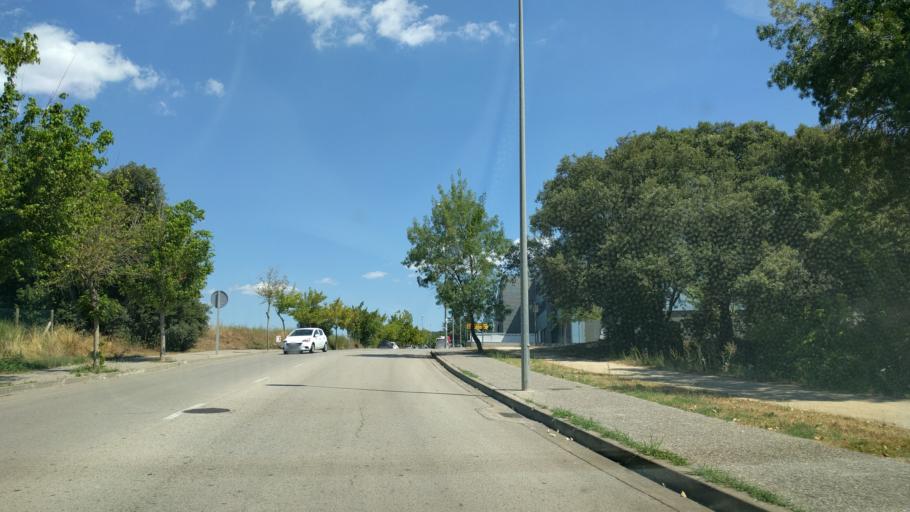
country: ES
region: Catalonia
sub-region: Provincia de Girona
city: Salt
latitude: 41.9913
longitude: 2.7952
